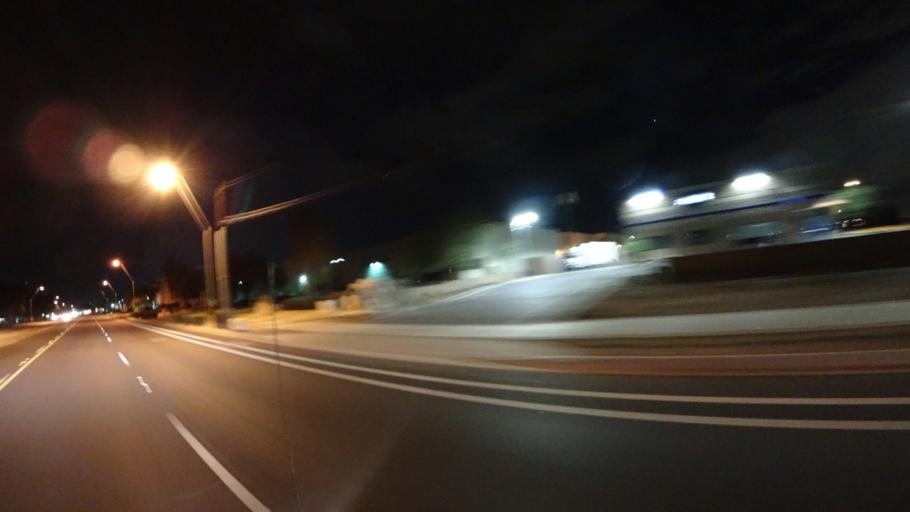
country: US
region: Arizona
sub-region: Maricopa County
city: Guadalupe
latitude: 33.3548
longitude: -111.9632
